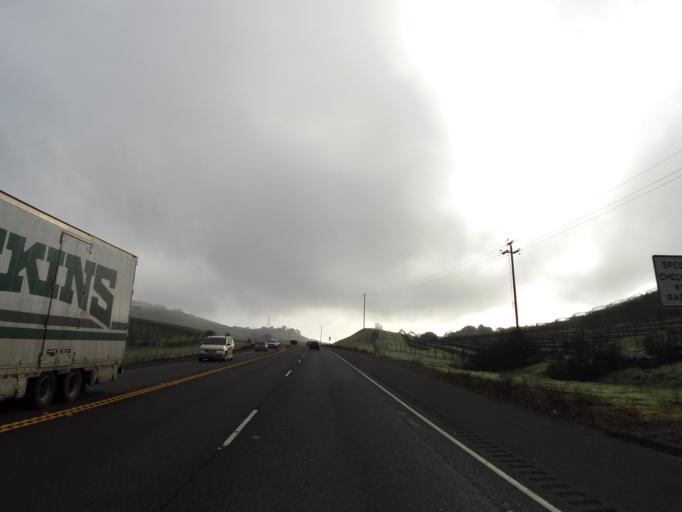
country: US
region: California
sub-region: Sonoma County
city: Sonoma
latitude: 38.2526
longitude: -122.3903
